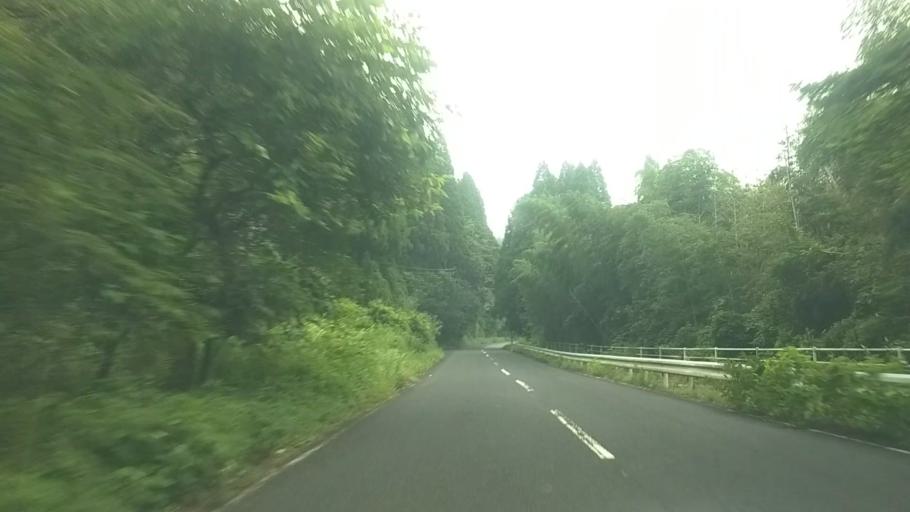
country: JP
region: Chiba
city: Katsuura
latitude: 35.2541
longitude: 140.2445
